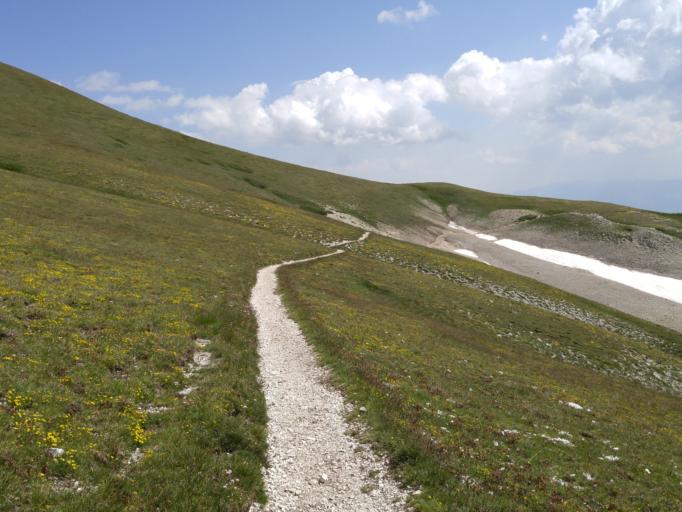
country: IT
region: Abruzzo
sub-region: Provincia di Teramo
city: Pietracamela
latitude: 42.4605
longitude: 13.5641
